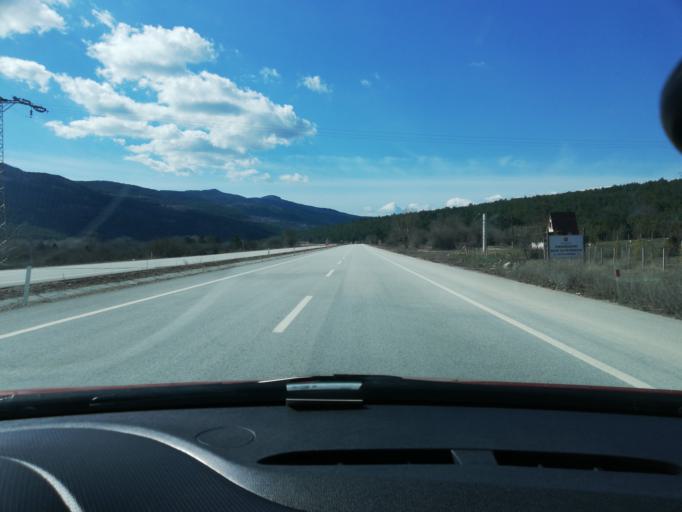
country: TR
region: Karabuk
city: Ovacik
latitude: 41.2012
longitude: 32.8513
